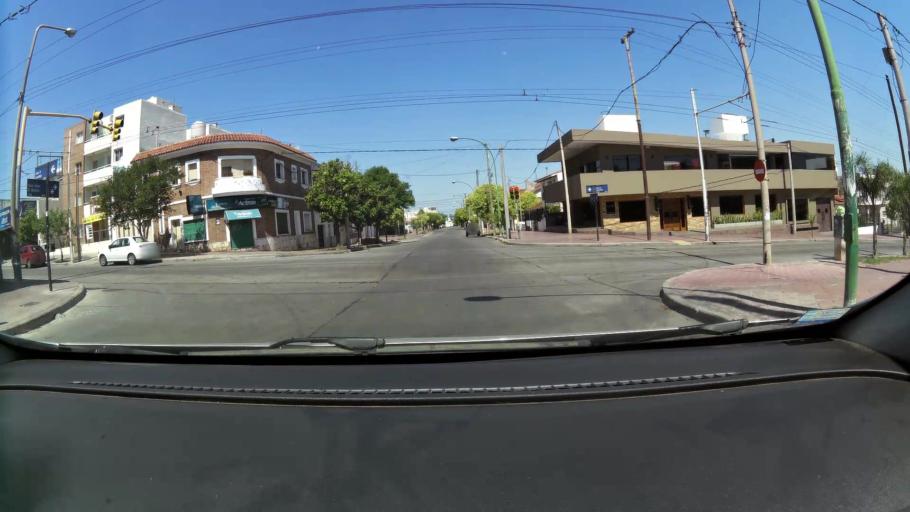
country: AR
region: Cordoba
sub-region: Departamento de Capital
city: Cordoba
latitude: -31.4016
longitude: -64.1870
